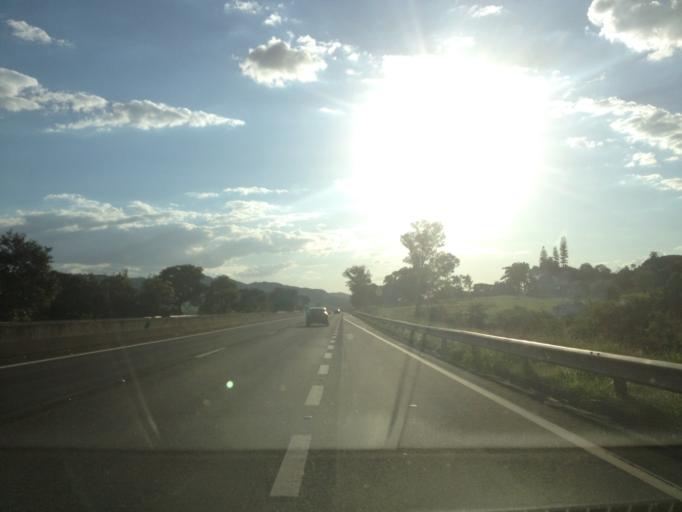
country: BR
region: Sao Paulo
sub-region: Brotas
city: Brotas
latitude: -22.2652
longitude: -48.2172
